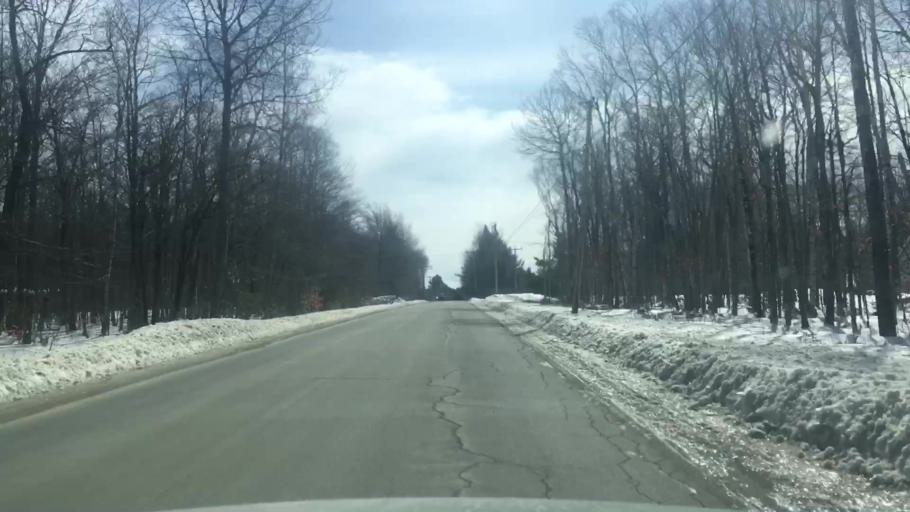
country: US
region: Maine
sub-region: Penobscot County
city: Holden
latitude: 44.7712
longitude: -68.6490
